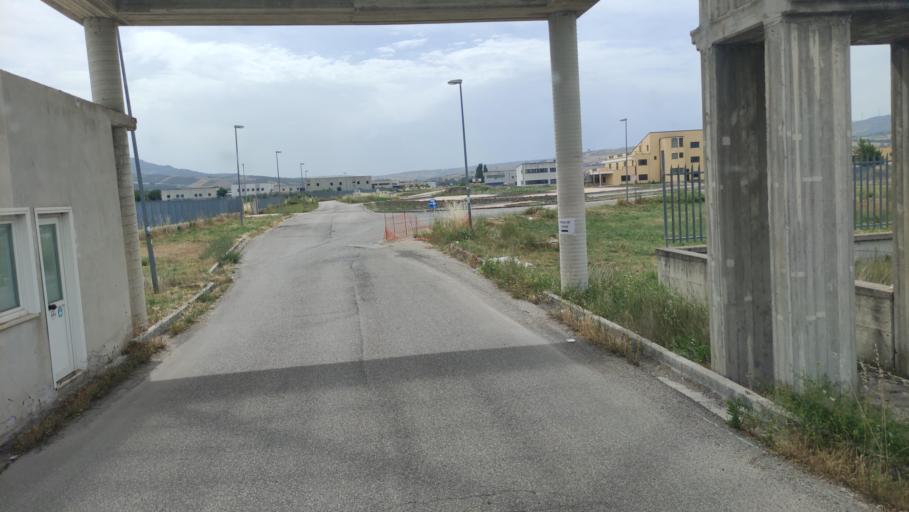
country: IT
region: Campania
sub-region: Provincia di Avellino
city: Sturno
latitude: 41.0514
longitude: 15.1212
